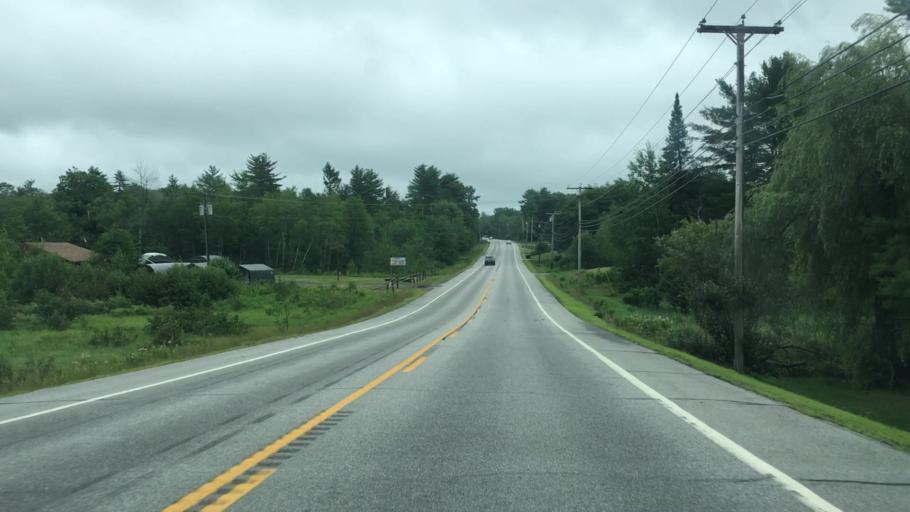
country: US
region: Maine
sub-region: Kennebec County
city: Chelsea
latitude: 44.2835
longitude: -69.6948
